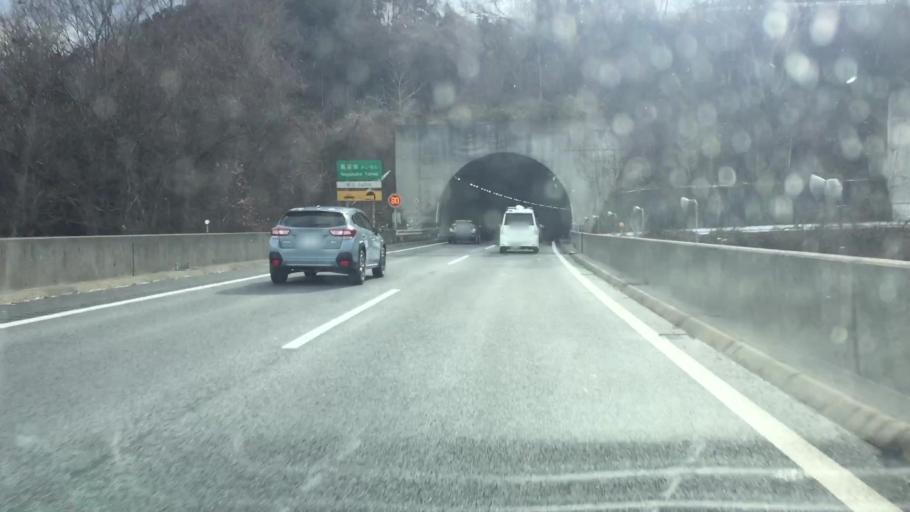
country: JP
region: Gunma
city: Numata
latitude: 36.5869
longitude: 139.0667
